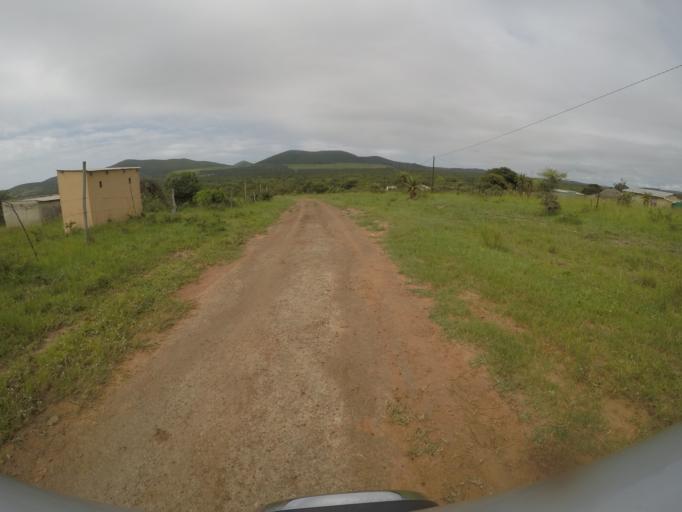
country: ZA
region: KwaZulu-Natal
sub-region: uThungulu District Municipality
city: Empangeni
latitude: -28.6161
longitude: 31.8462
